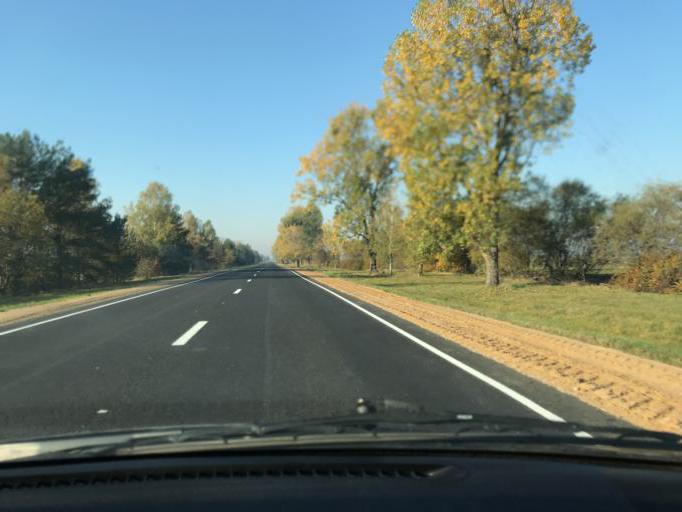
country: BY
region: Brest
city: Baranovichi
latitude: 52.9014
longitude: 25.8781
